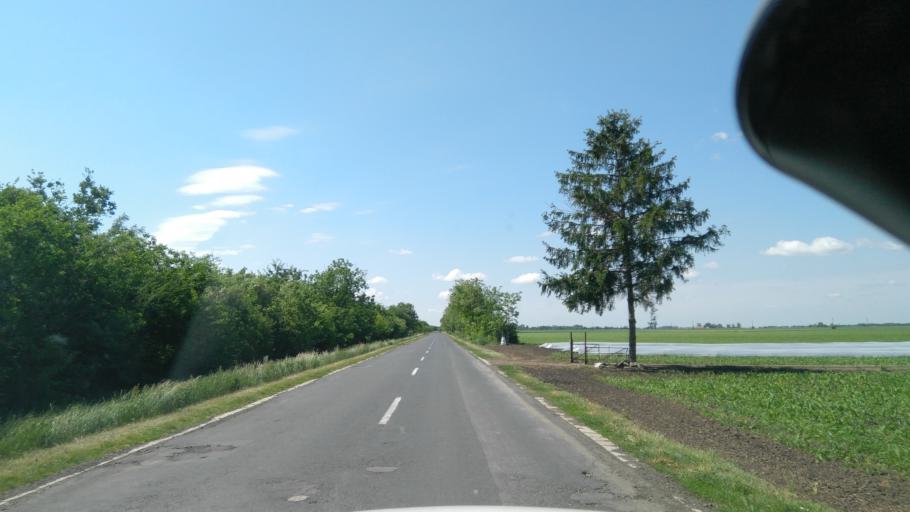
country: HU
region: Bekes
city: Medgyesegyhaza
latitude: 46.4828
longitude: 21.0229
